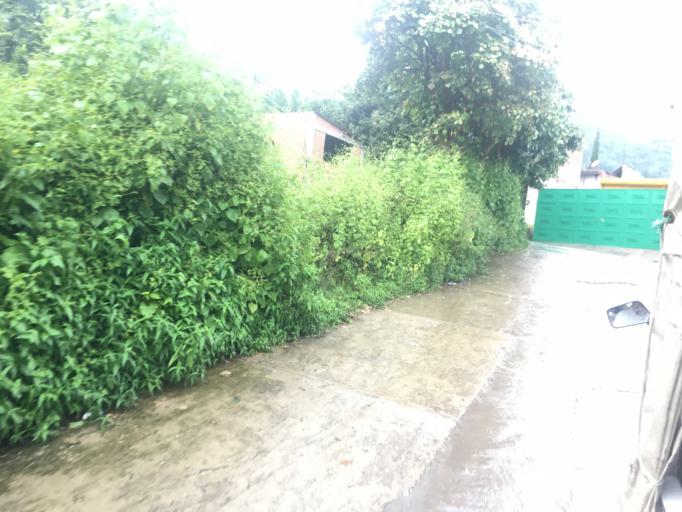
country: MX
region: Morelos
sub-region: Tlayacapan
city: Tlayacapan
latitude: 18.9529
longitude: -98.9913
